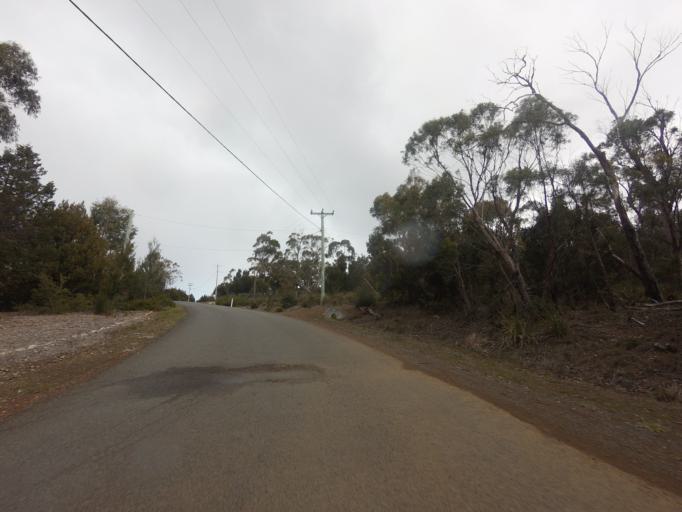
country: AU
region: Tasmania
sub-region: Sorell
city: Sorell
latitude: -42.5332
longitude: 147.9123
